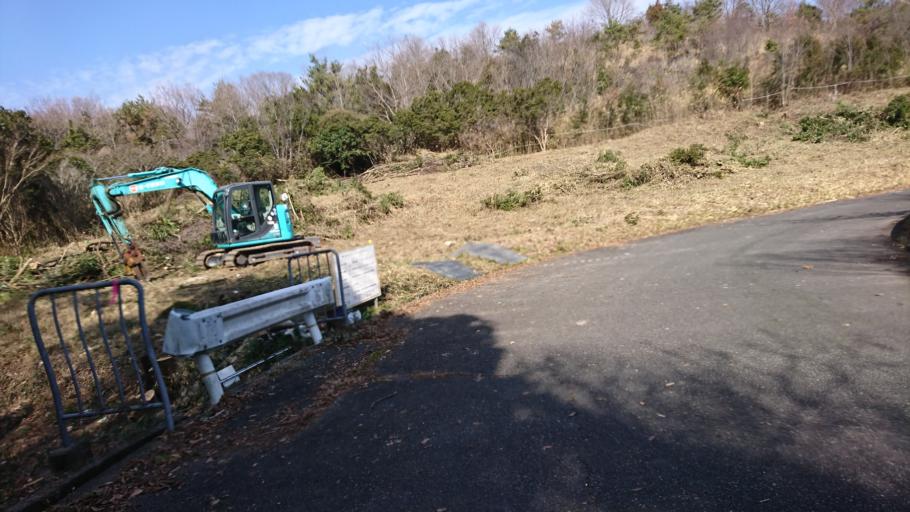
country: JP
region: Hyogo
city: Kakogawacho-honmachi
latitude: 34.8216
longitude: 134.8673
